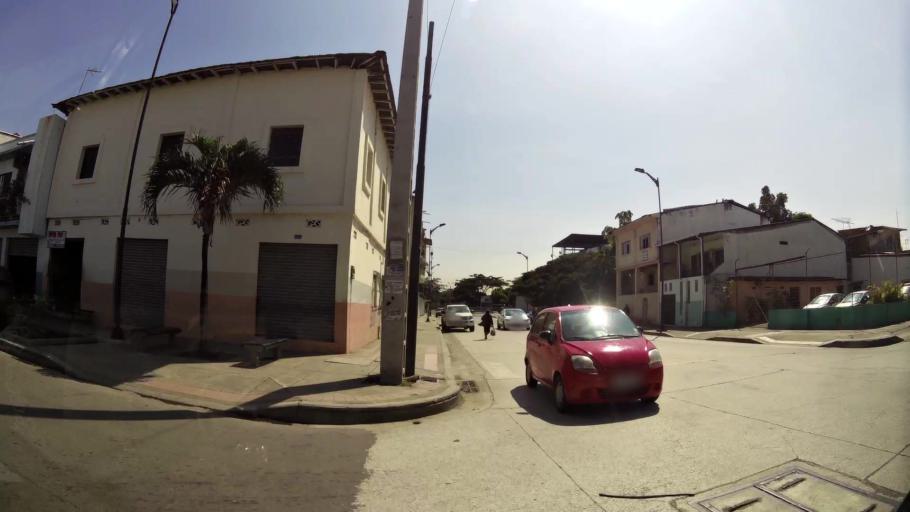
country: EC
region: Guayas
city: Guayaquil
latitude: -2.1905
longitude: -79.9009
